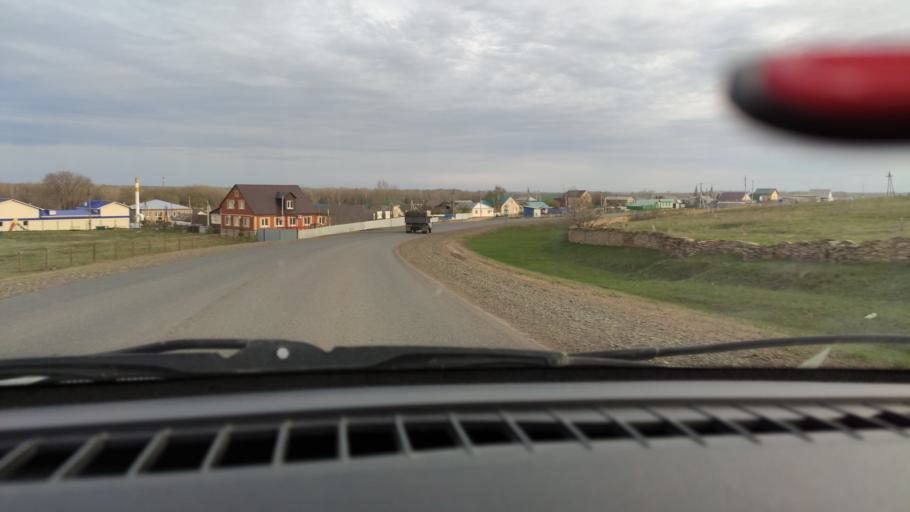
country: RU
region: Orenburg
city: Tatarskaya Kargala
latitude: 51.9499
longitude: 55.1817
